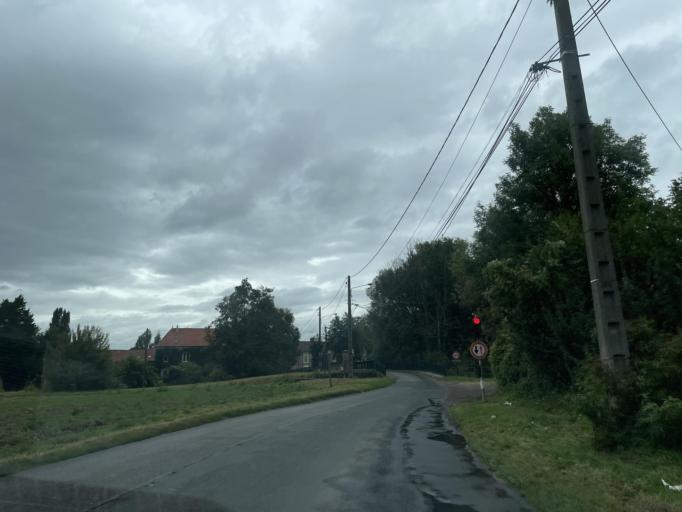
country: FR
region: Ile-de-France
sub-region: Departement de Seine-et-Marne
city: Chailly-en-Brie
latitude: 48.8097
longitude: 3.1123
